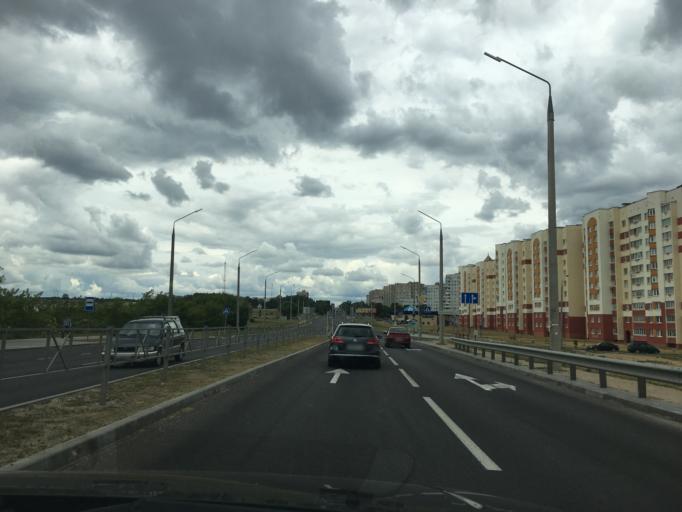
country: BY
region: Grodnenskaya
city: Hrodna
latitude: 53.6382
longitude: 23.8475
